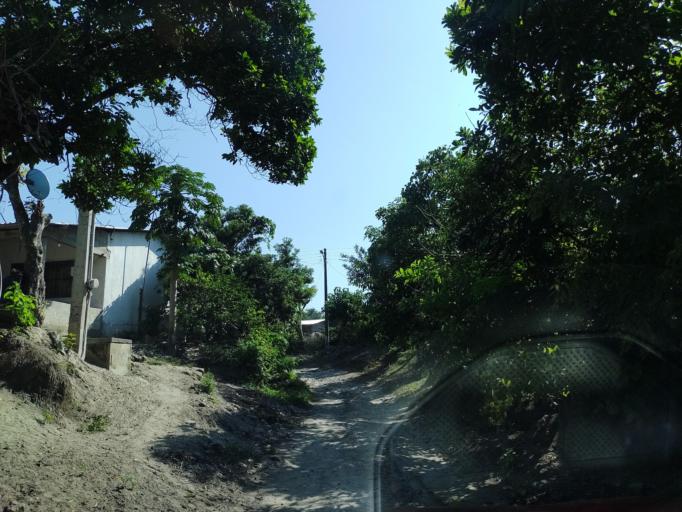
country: MX
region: Veracruz
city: Agua Dulce
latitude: 20.2558
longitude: -97.2509
